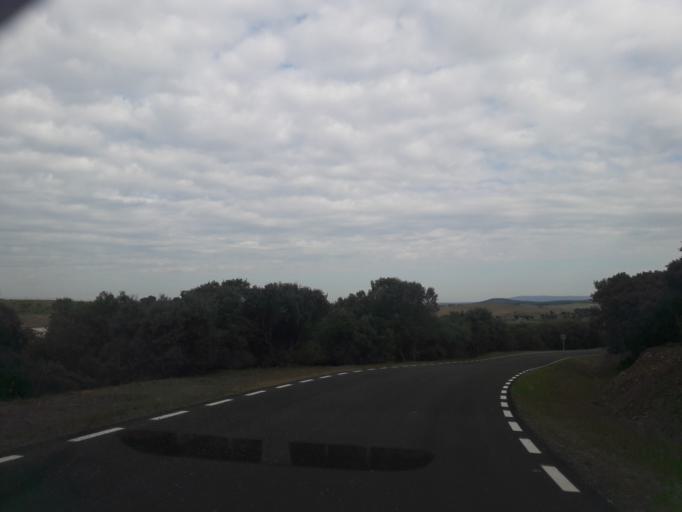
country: ES
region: Castille and Leon
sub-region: Provincia de Salamanca
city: Pastores
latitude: 40.5253
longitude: -6.5251
